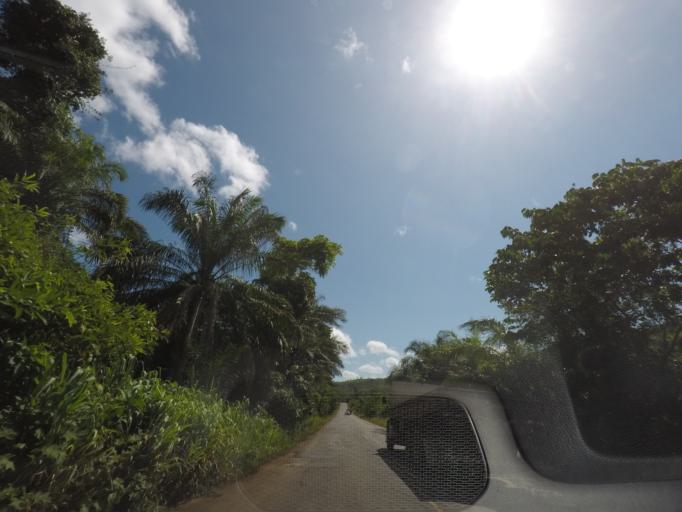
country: BR
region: Bahia
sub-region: Itubera
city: Itubera
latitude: -13.6871
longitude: -39.1296
